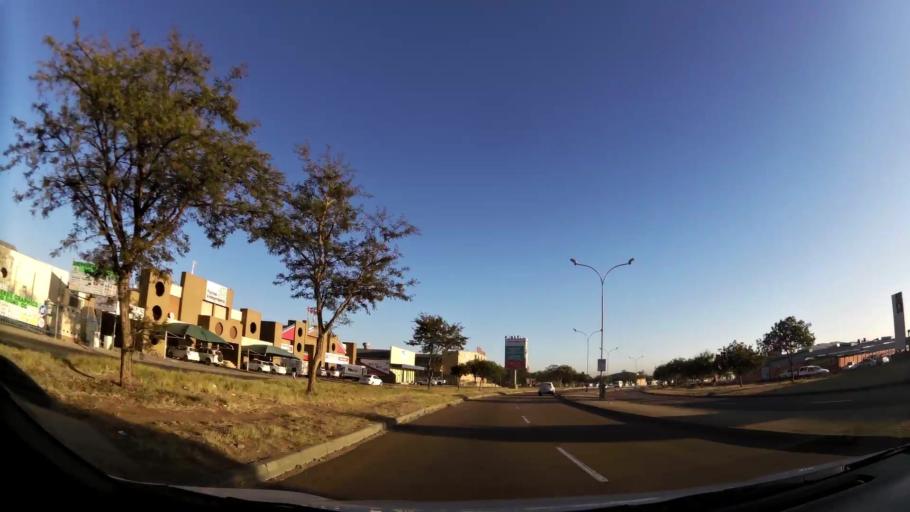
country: ZA
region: Limpopo
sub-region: Capricorn District Municipality
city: Polokwane
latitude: -23.9128
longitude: 29.4403
